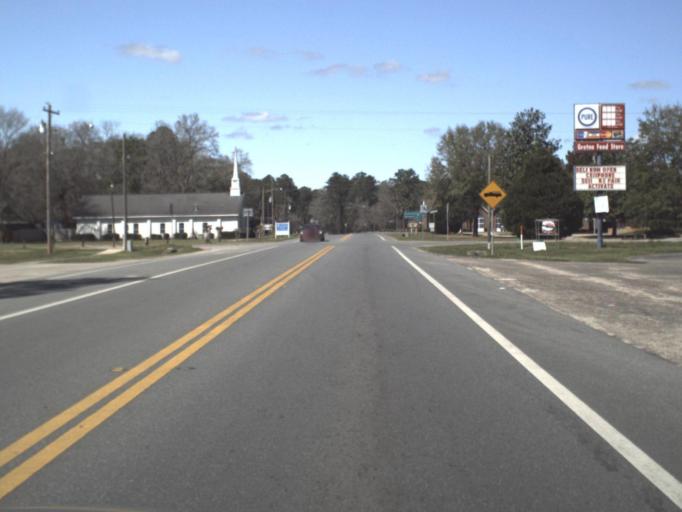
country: US
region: Florida
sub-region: Gadsden County
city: Gretna
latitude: 30.6177
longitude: -84.6629
